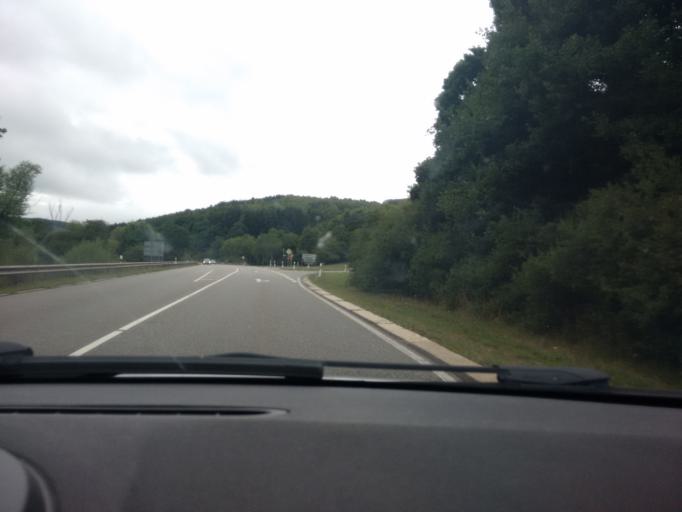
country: DE
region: Rheinland-Pfalz
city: Rotsweiler-Nockenthal
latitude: 49.7119
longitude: 7.2769
